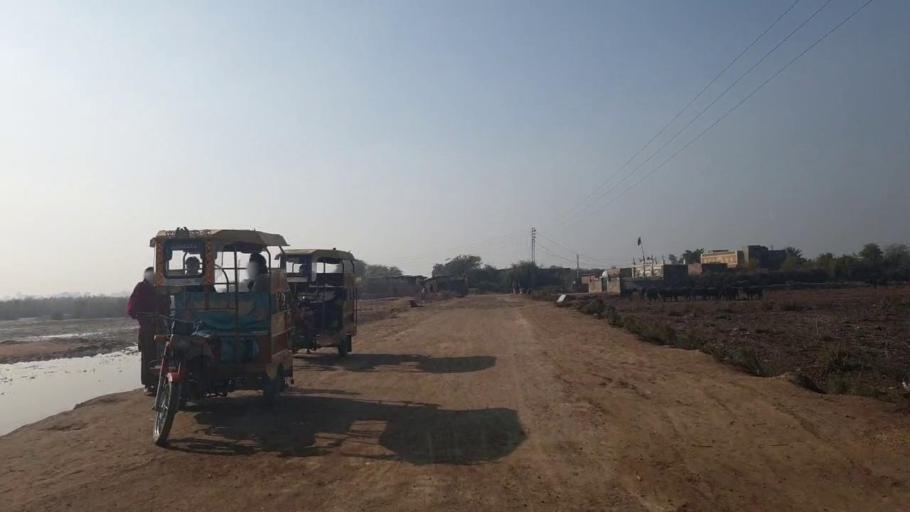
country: PK
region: Sindh
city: Shahdadpur
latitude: 25.9471
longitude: 68.5825
